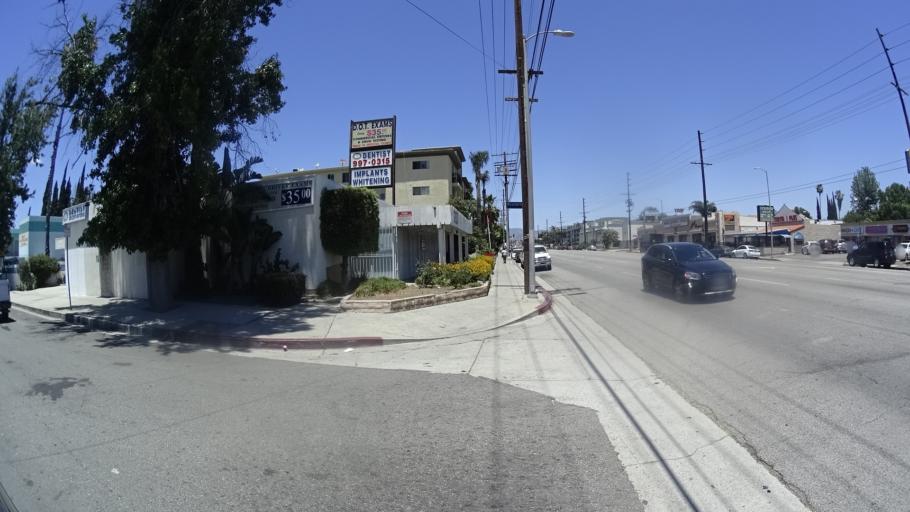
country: US
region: California
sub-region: Los Angeles County
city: Van Nuys
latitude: 34.2031
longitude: -118.4664
